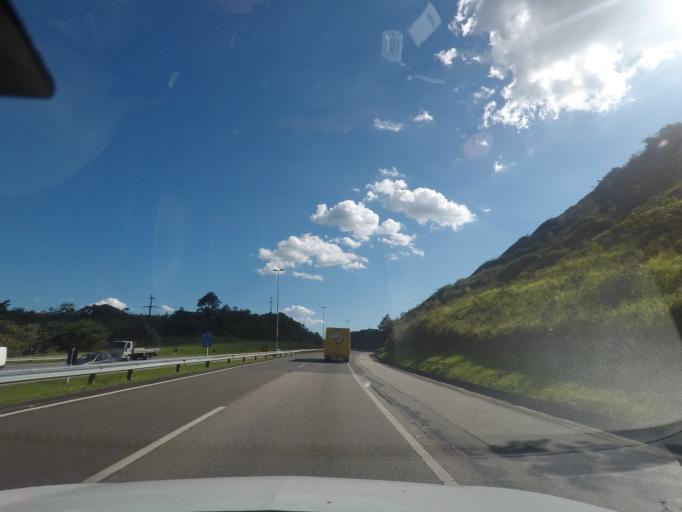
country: BR
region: Rio de Janeiro
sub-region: Guapimirim
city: Guapimirim
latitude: -22.5770
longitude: -43.0101
